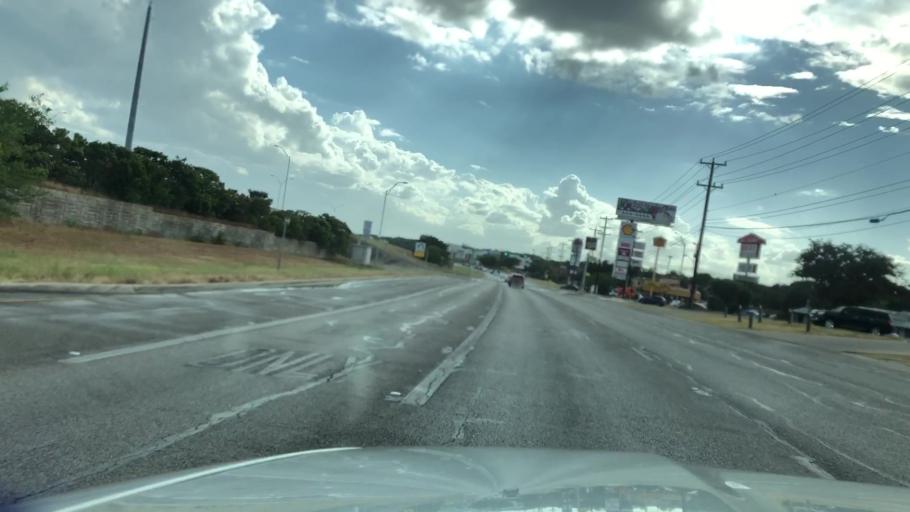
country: US
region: Texas
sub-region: Bexar County
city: Helotes
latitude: 29.5879
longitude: -98.6297
